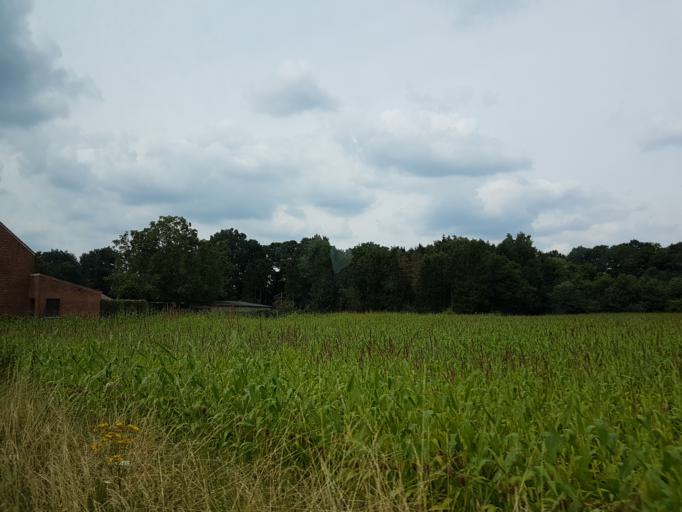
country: BE
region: Flanders
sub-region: Provincie Antwerpen
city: Olen
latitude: 51.1052
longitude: 4.8753
